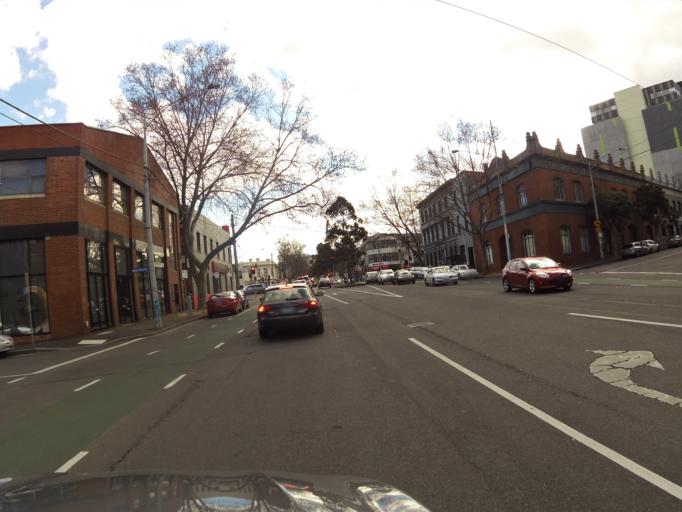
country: AU
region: Victoria
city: Carlton
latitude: -37.8042
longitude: 144.9597
